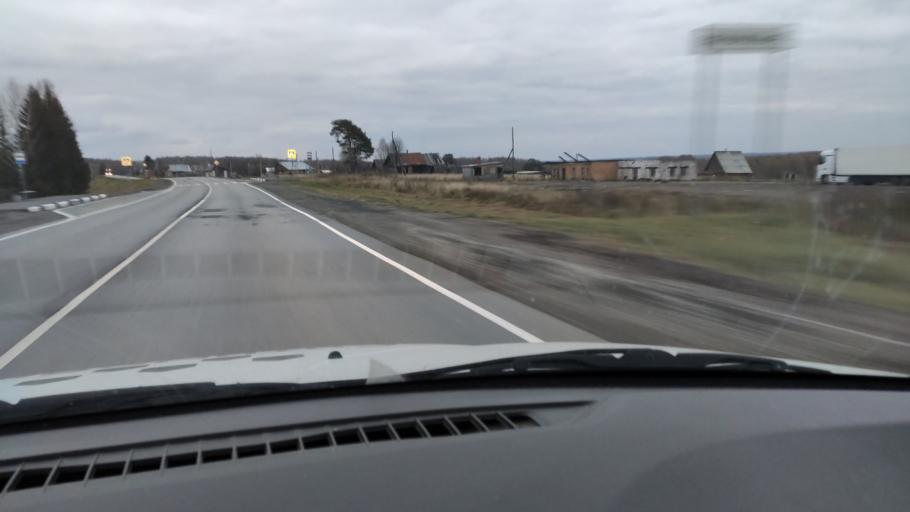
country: RU
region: Kirov
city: Kostino
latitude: 58.7951
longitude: 52.8857
